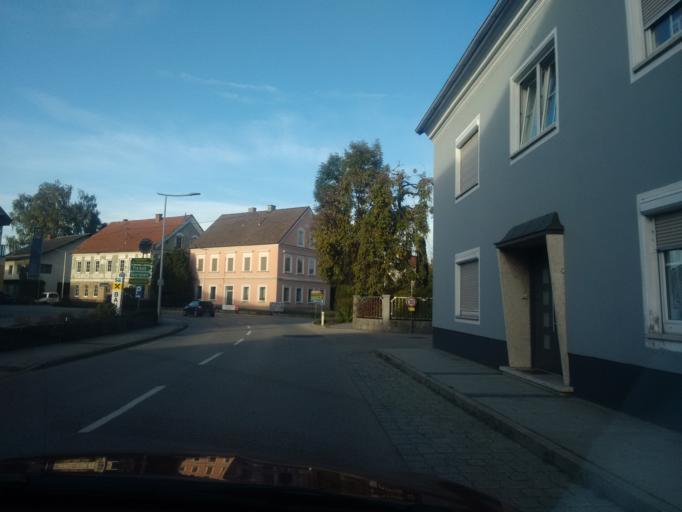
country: AT
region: Upper Austria
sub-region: Politischer Bezirk Vocklabruck
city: Niederthalheim
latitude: 48.1414
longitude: 13.7368
